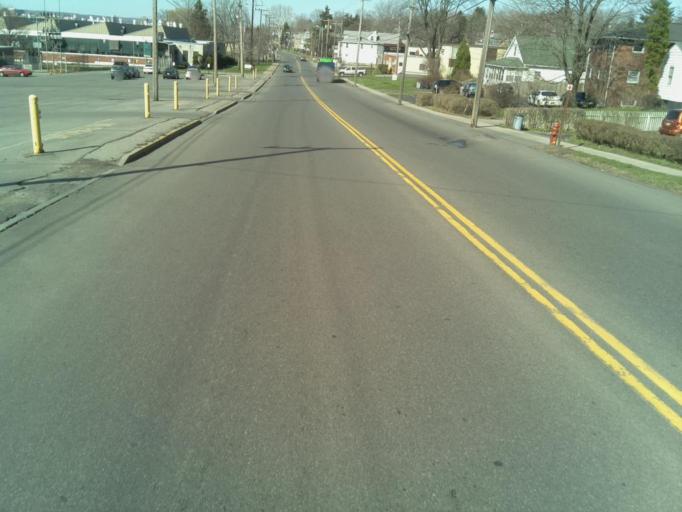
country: US
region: New York
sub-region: Onondaga County
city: Lyncourt
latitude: 43.0571
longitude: -76.1100
